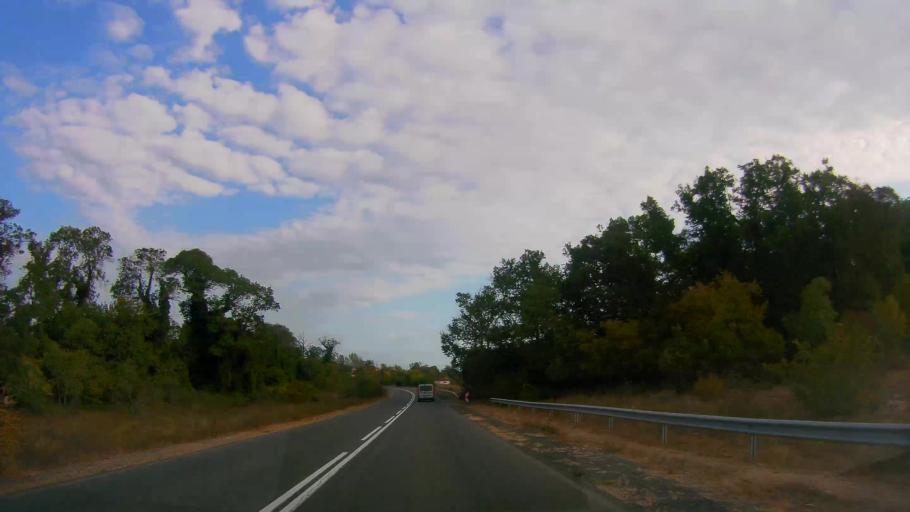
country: BG
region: Burgas
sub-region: Obshtina Primorsko
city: Primorsko
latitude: 42.3253
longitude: 27.7305
